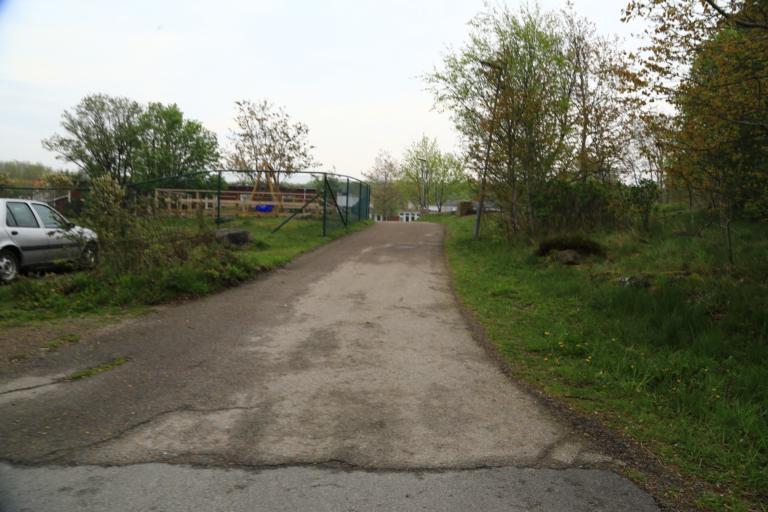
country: SE
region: Halland
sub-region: Varbergs Kommun
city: Varberg
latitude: 57.0958
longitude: 12.2639
